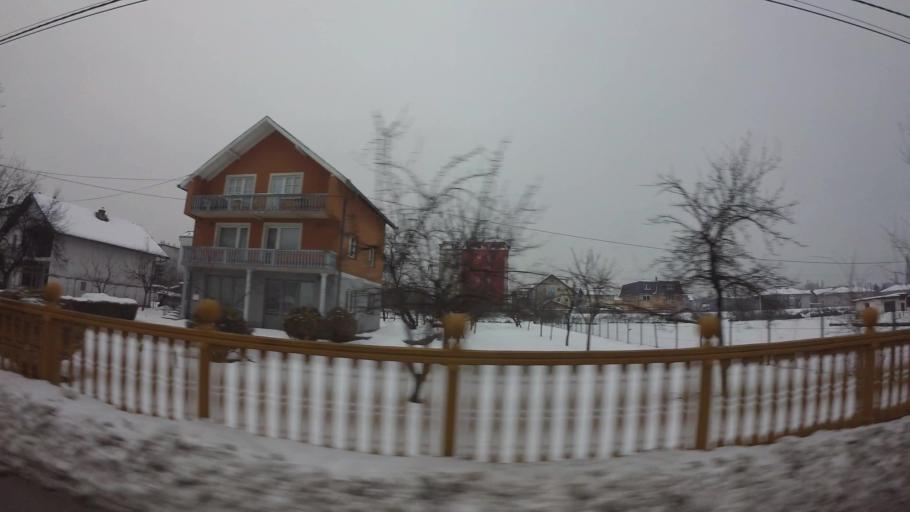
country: BA
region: Federation of Bosnia and Herzegovina
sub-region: Kanton Sarajevo
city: Sarajevo
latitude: 43.8423
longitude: 18.3131
